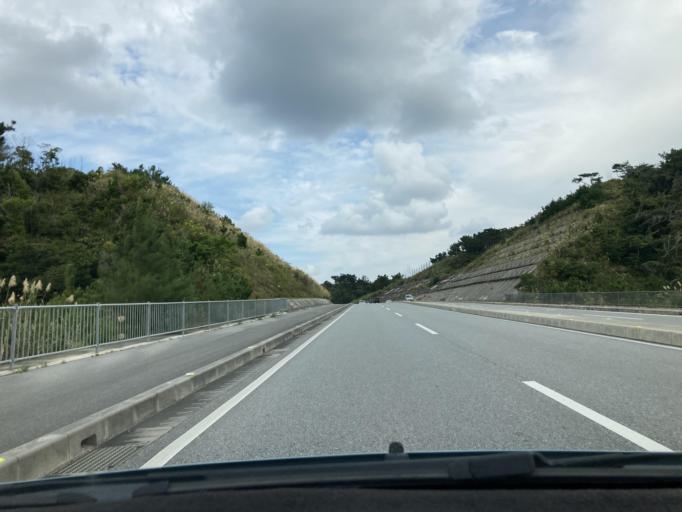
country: JP
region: Okinawa
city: Ishikawa
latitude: 26.4709
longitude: 127.8364
